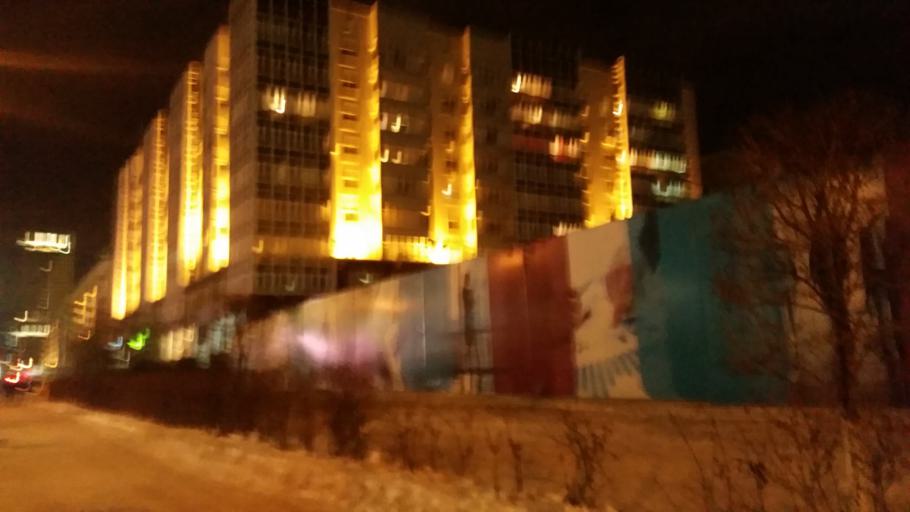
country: KZ
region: Astana Qalasy
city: Astana
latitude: 51.1271
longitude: 71.4215
